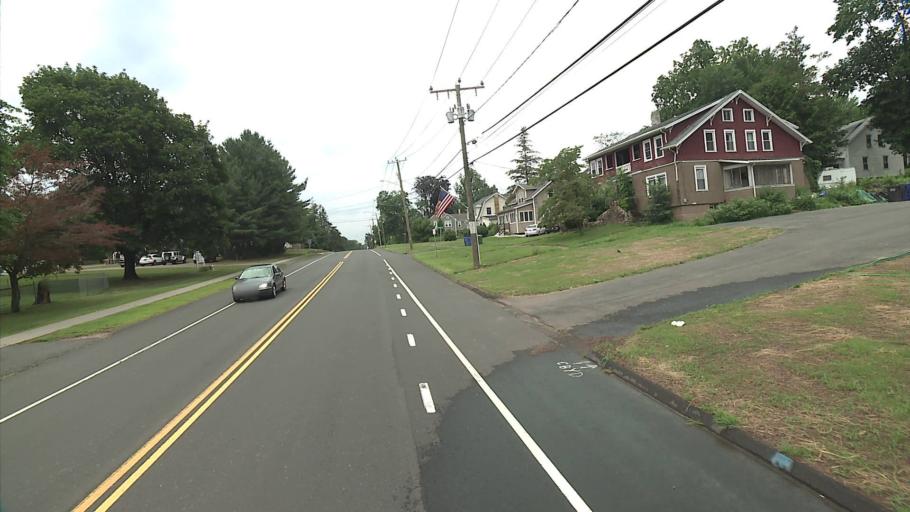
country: US
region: Connecticut
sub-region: Middlesex County
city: Cromwell
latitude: 41.6092
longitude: -72.6502
